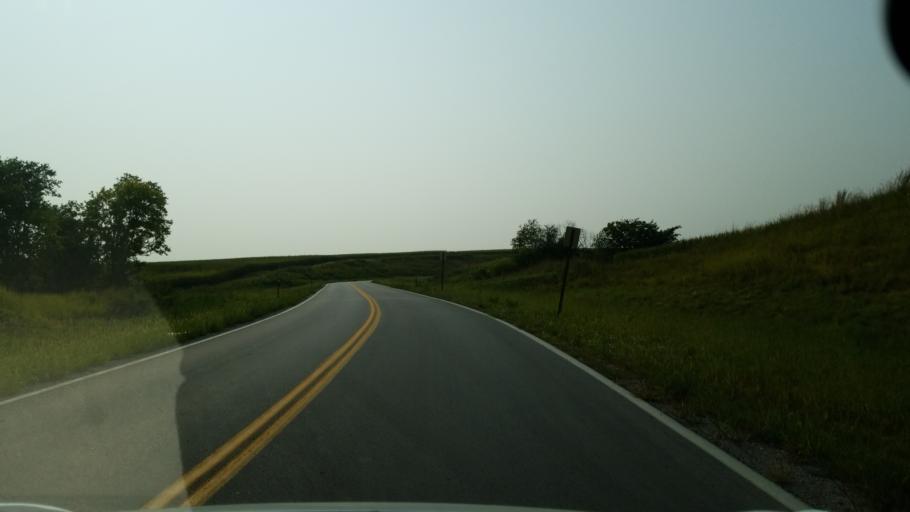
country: US
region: Nebraska
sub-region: Sarpy County
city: Offutt Air Force Base
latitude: 41.0803
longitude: -95.9326
